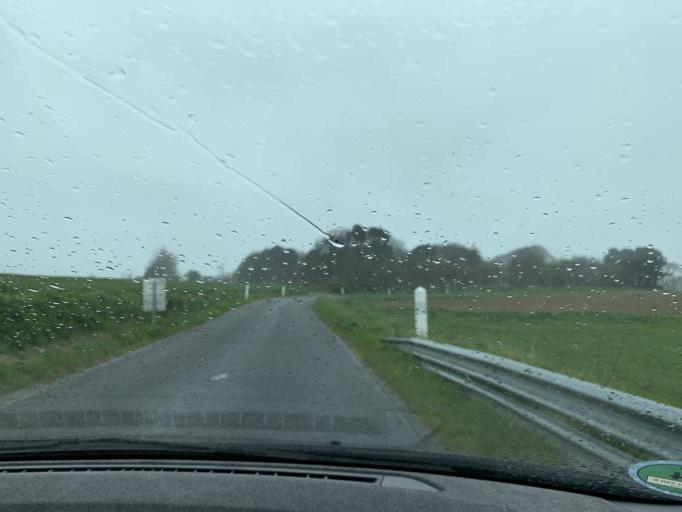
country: FR
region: Haute-Normandie
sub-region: Departement de la Seine-Maritime
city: Etretat
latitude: 49.7133
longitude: 0.2382
